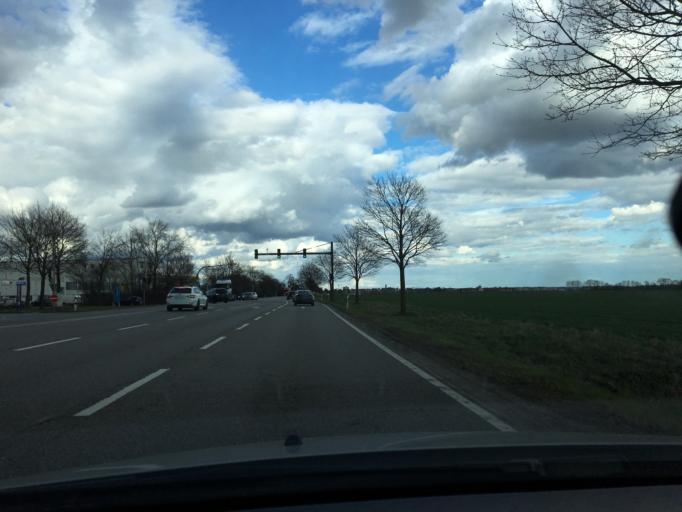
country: DE
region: Bavaria
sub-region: Upper Bavaria
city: Eching
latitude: 48.3022
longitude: 11.6351
